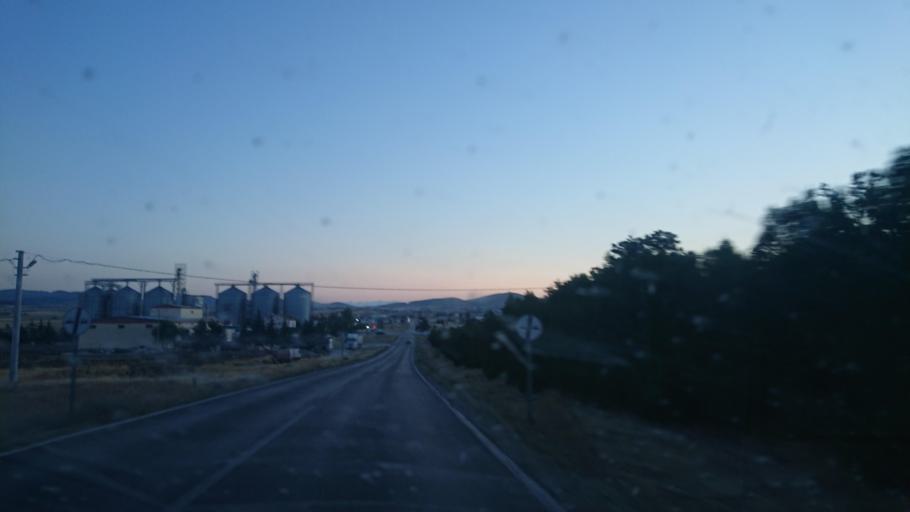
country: TR
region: Aksaray
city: Balci
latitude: 38.7634
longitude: 34.0897
